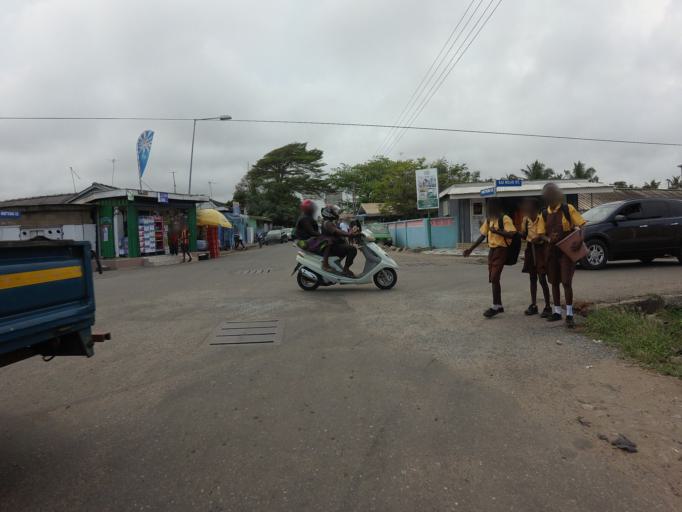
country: GH
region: Greater Accra
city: Accra
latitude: 5.5543
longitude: -0.1773
